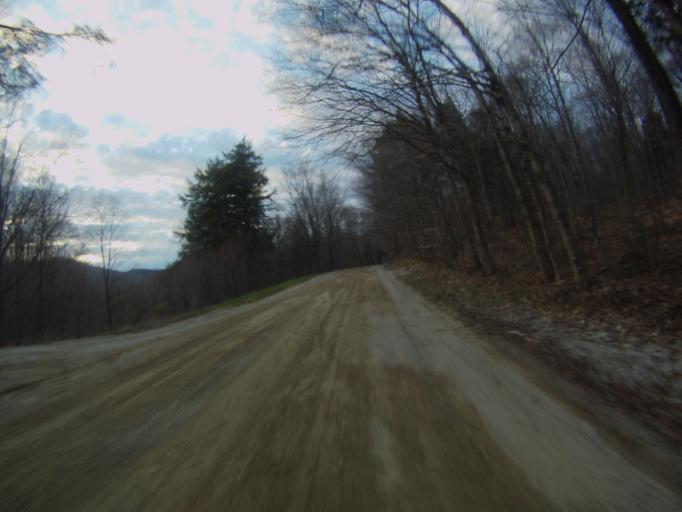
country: US
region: Vermont
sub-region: Rutland County
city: Brandon
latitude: 43.9227
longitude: -73.0191
